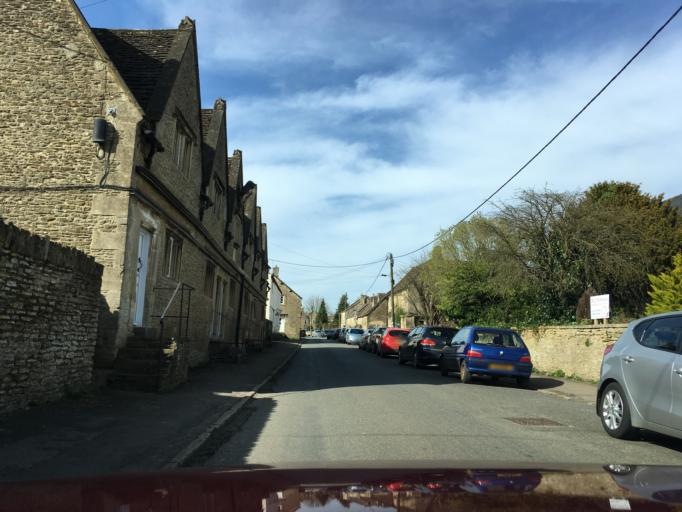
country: GB
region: England
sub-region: Wiltshire
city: Chippenham
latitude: 51.4949
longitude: -2.1394
